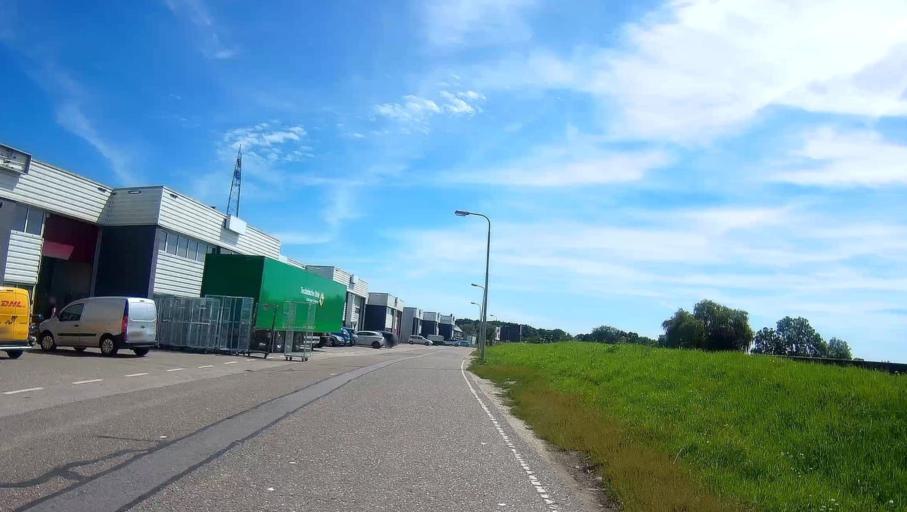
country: NL
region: South Holland
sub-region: Gemeente Ridderkerk
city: Ridderkerk
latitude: 51.8942
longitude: 4.5871
